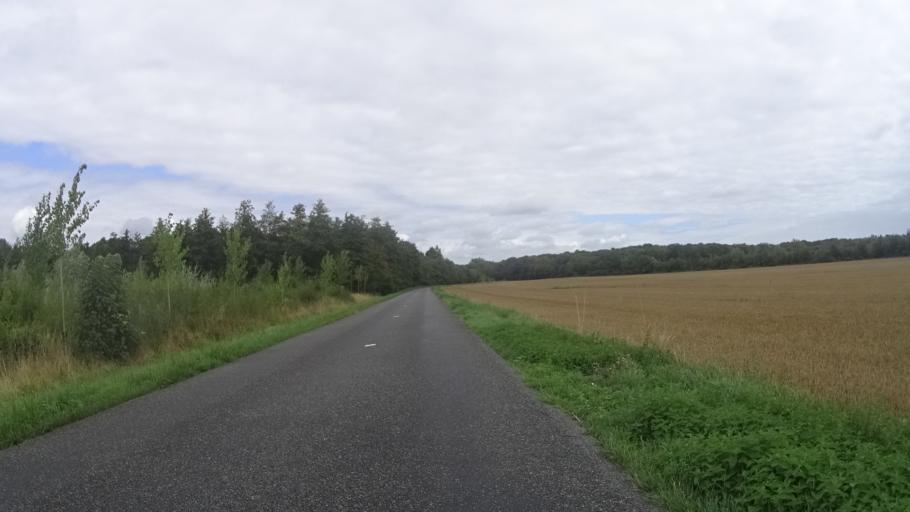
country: FR
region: Picardie
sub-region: Departement de l'Oise
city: Chiry-Ourscamp
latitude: 49.5369
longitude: 2.9729
